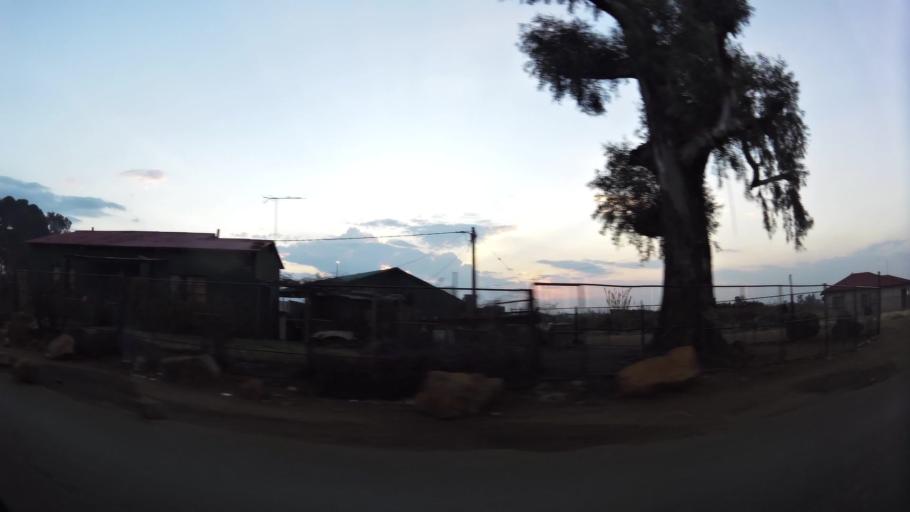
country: ZA
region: Gauteng
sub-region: City of Johannesburg Metropolitan Municipality
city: Orange Farm
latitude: -26.5546
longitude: 27.8804
